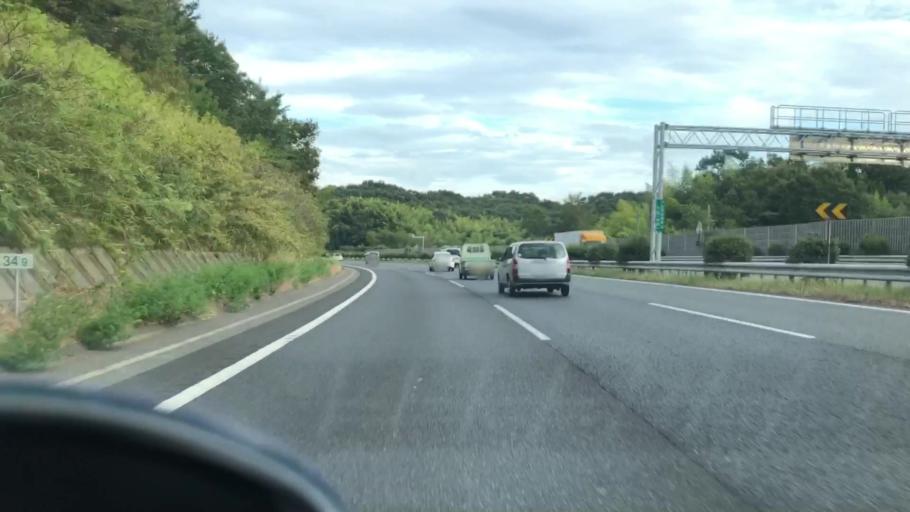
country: JP
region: Hyogo
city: Sandacho
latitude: 34.8687
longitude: 135.1997
